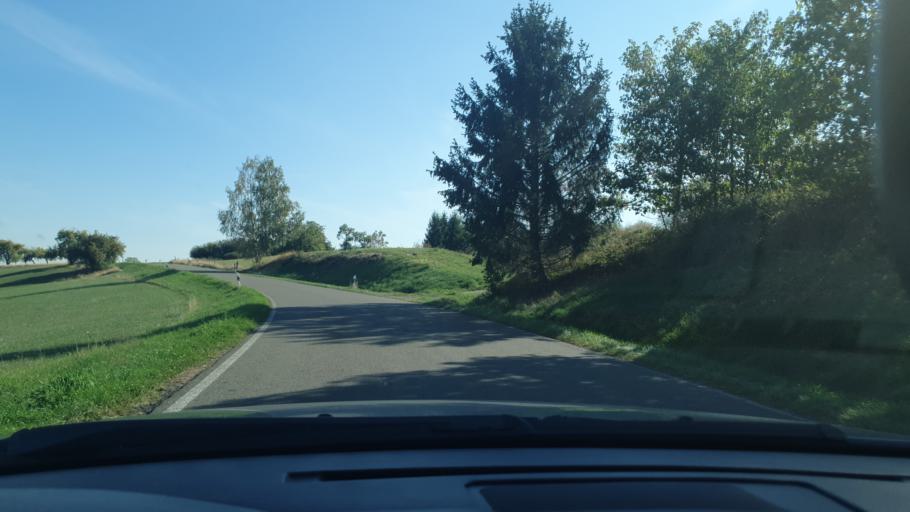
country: DE
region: Rheinland-Pfalz
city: Grossbundenbach
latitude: 49.3007
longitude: 7.4248
